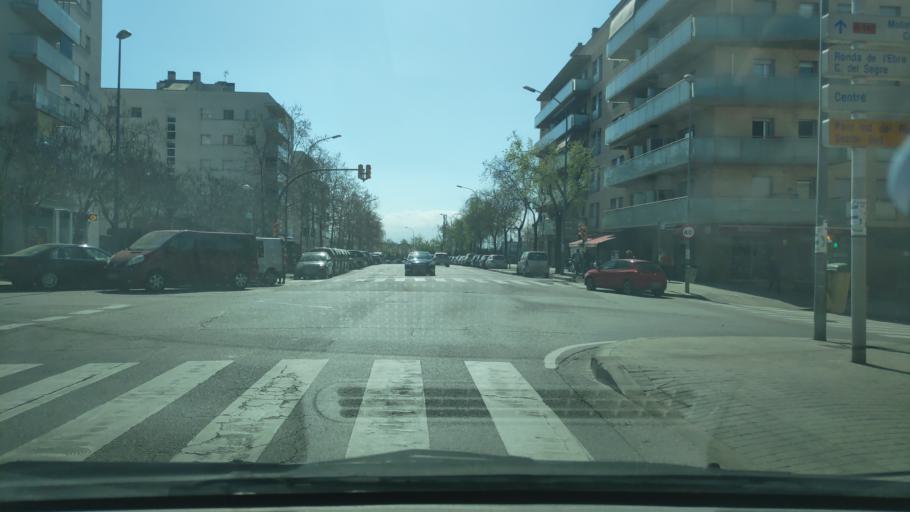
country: ES
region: Catalonia
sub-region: Provincia de Barcelona
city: Sabadell
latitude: 41.5471
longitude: 2.1284
